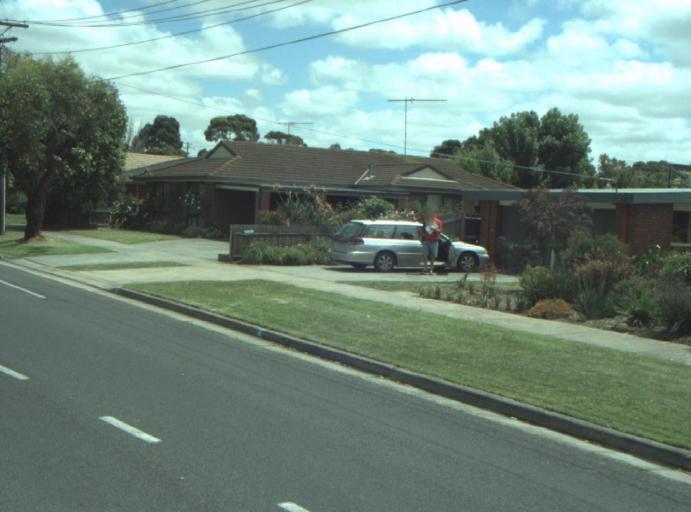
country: AU
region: Victoria
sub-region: Greater Geelong
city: Breakwater
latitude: -38.1885
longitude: 144.3432
